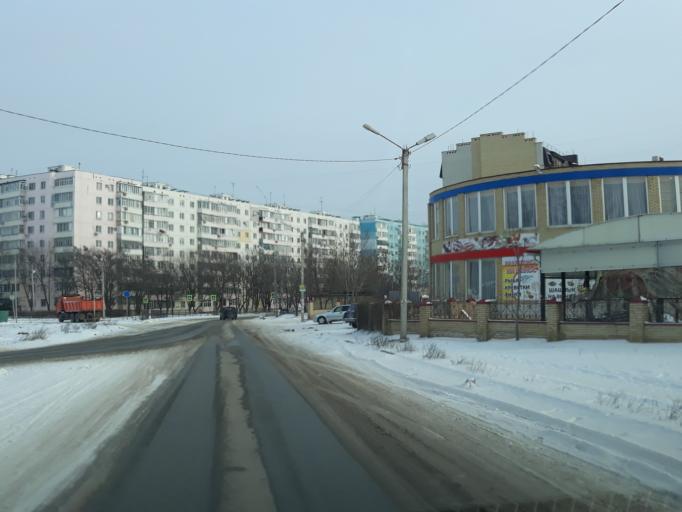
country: RU
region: Rostov
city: Taganrog
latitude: 47.2255
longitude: 38.8568
